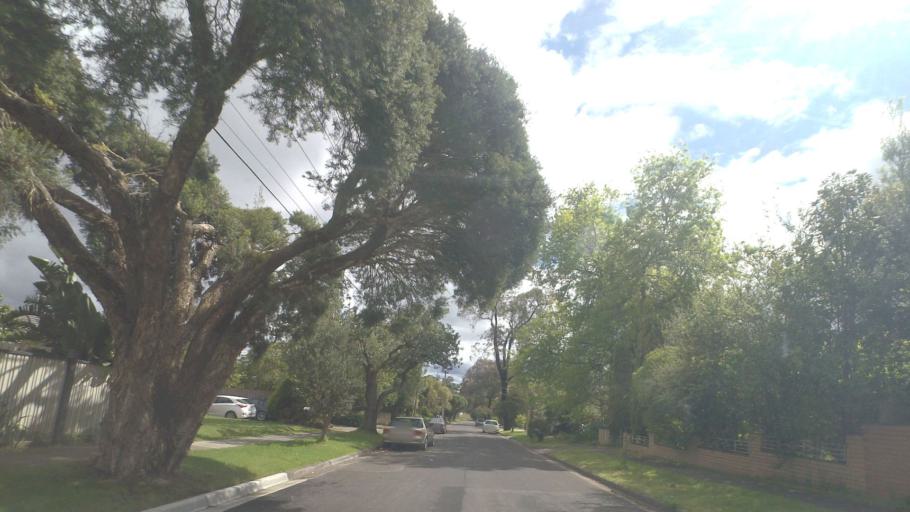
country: AU
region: Victoria
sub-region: Maroondah
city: Heathmont
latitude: -37.8433
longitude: 145.2405
